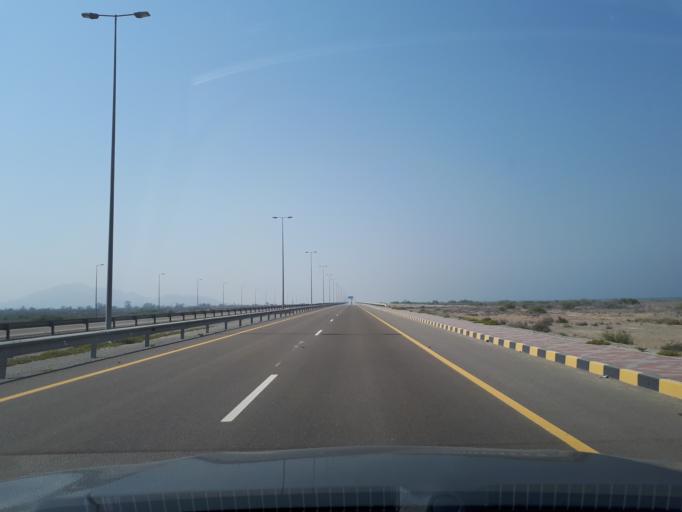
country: AE
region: Al Fujayrah
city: Al Fujayrah
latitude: 24.9352
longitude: 56.3832
